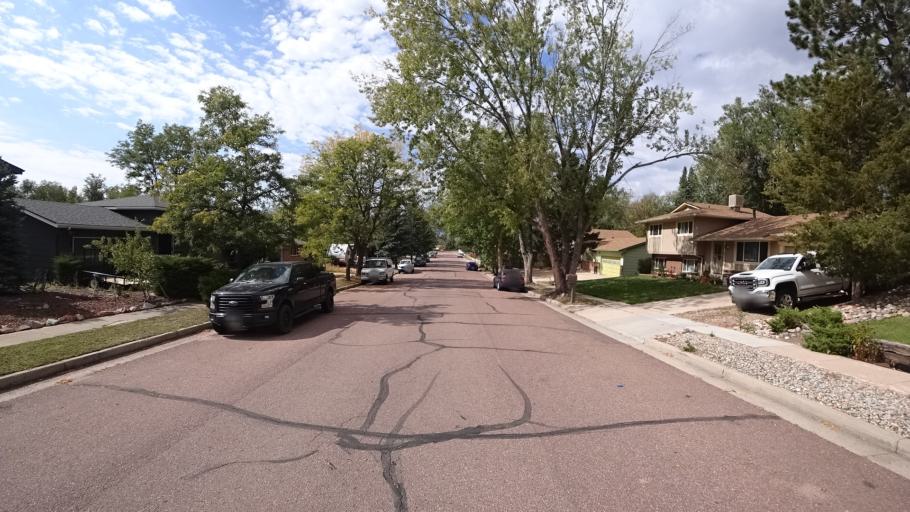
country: US
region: Colorado
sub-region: El Paso County
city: Cimarron Hills
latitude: 38.8561
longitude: -104.7350
